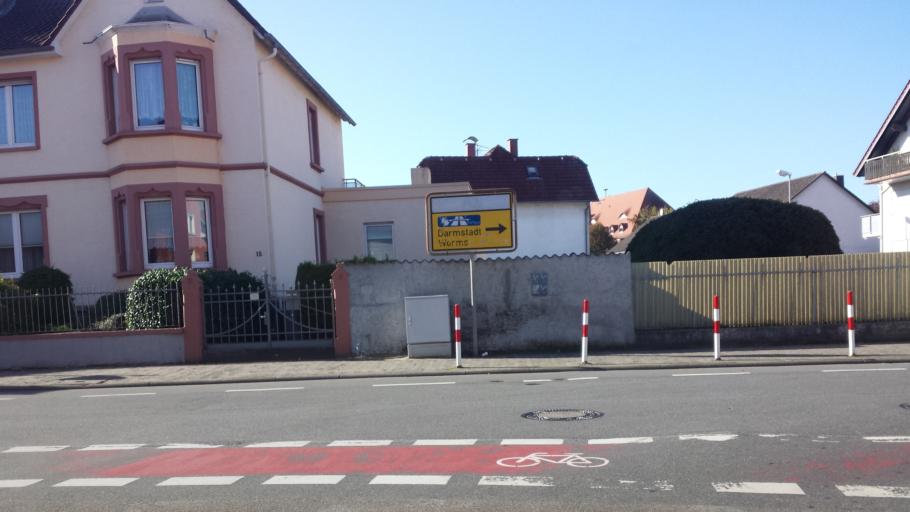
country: DE
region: Hesse
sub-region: Regierungsbezirk Darmstadt
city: Bensheim
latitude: 49.6773
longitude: 8.6228
